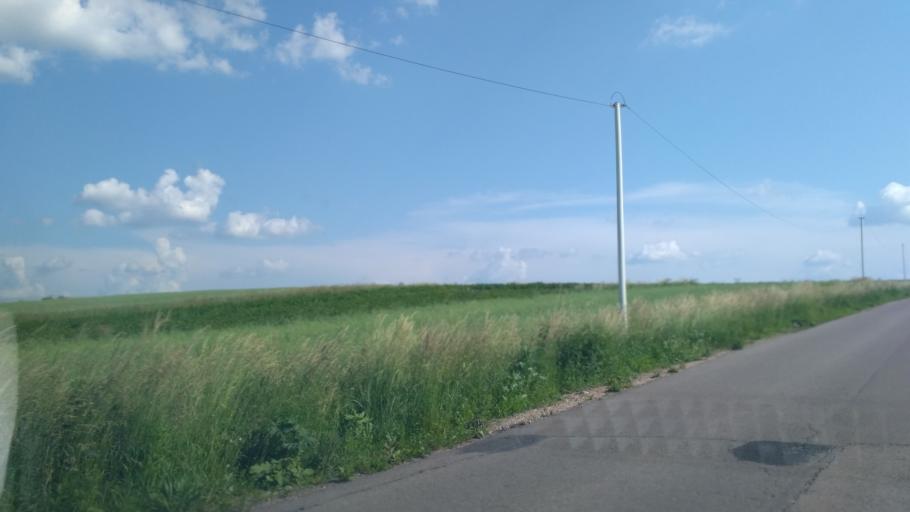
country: PL
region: Subcarpathian Voivodeship
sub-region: Powiat jaroslawski
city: Ostrow
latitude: 49.9358
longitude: 22.7398
